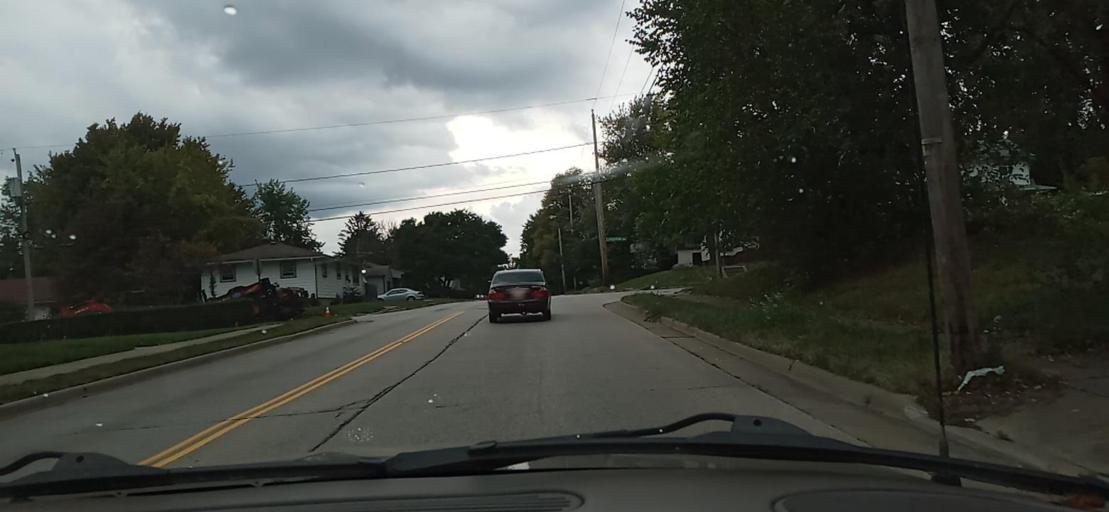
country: US
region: Ohio
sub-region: Summit County
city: Akron
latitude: 41.0643
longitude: -81.5583
